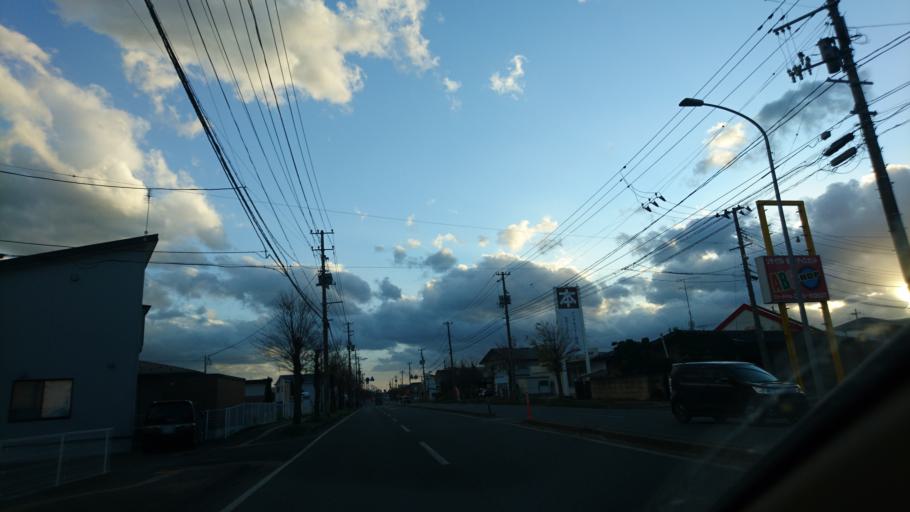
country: JP
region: Iwate
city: Mizusawa
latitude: 39.1508
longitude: 141.1327
